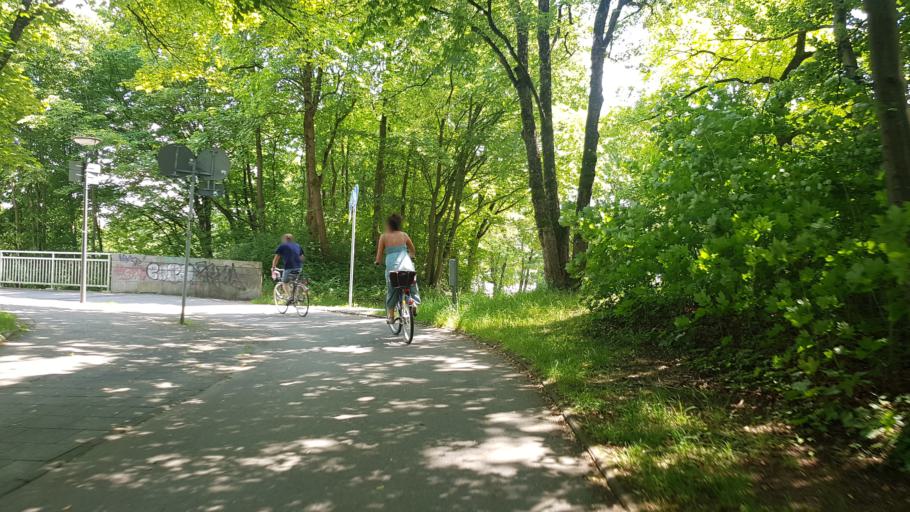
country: DE
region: Bavaria
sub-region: Upper Bavaria
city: Neuried
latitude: 48.1010
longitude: 11.5024
